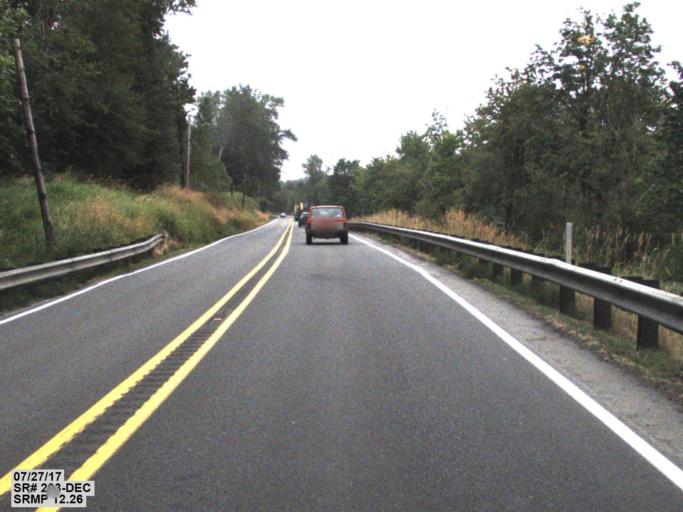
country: US
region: Washington
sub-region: King County
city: Duvall
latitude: 47.7040
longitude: -121.9834
